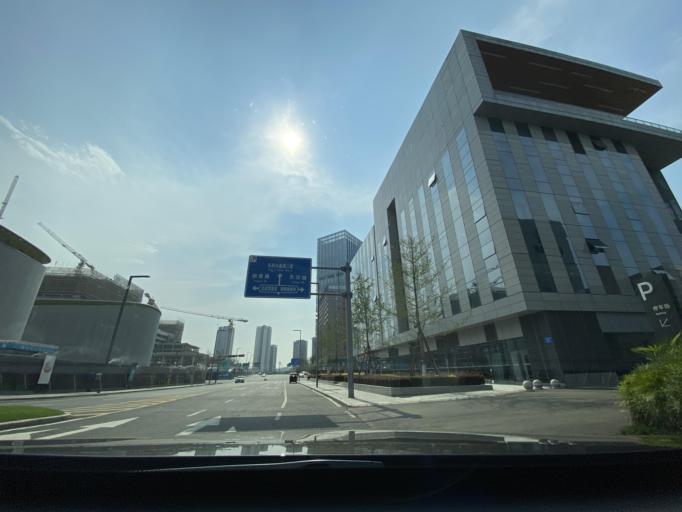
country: CN
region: Sichuan
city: Dongsheng
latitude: 30.3958
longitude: 104.0745
